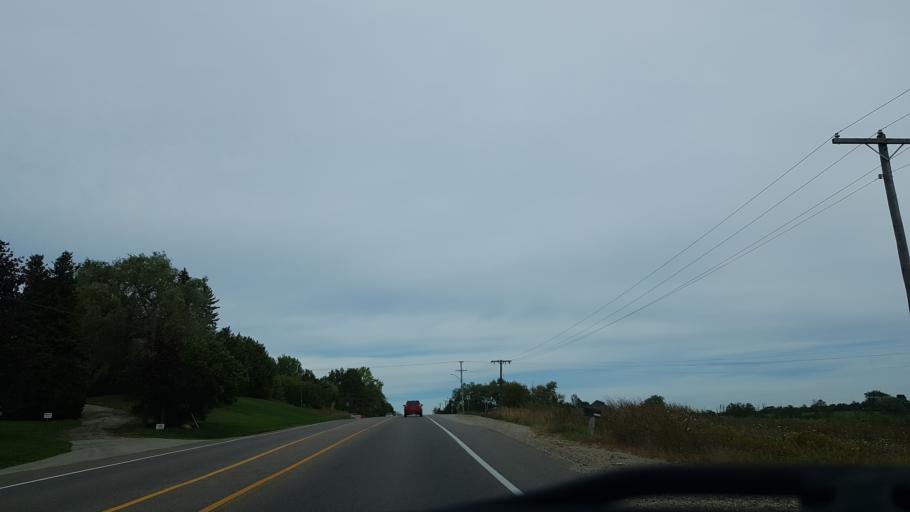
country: CA
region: Ontario
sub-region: Wellington County
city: Guelph
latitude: 43.5893
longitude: -80.2424
